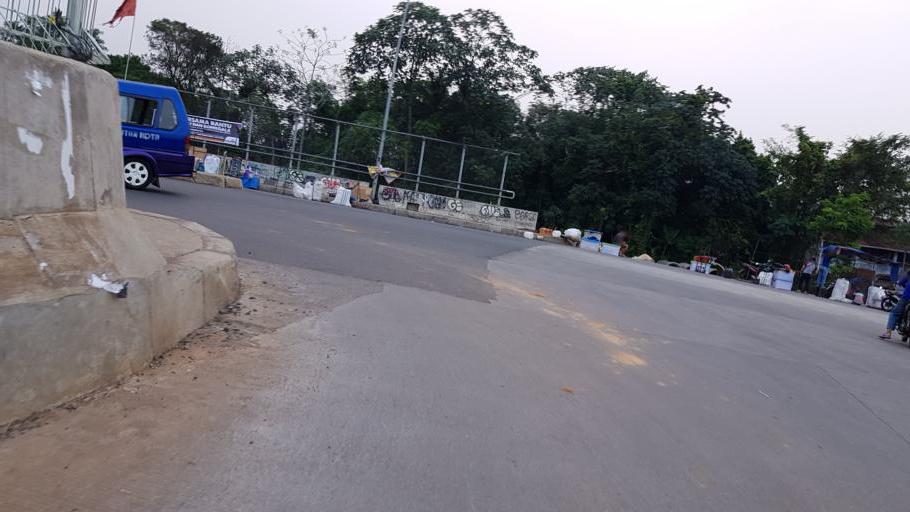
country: ID
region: West Java
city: Depok
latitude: -6.3691
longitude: 106.8137
